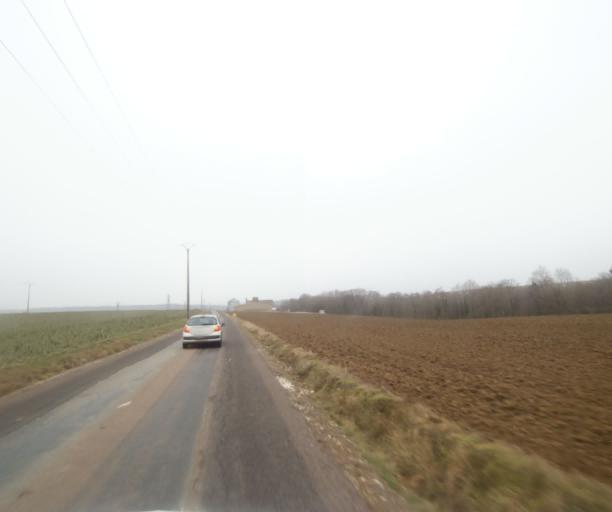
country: FR
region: Champagne-Ardenne
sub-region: Departement de la Haute-Marne
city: Bienville
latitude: 48.5414
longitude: 5.0658
